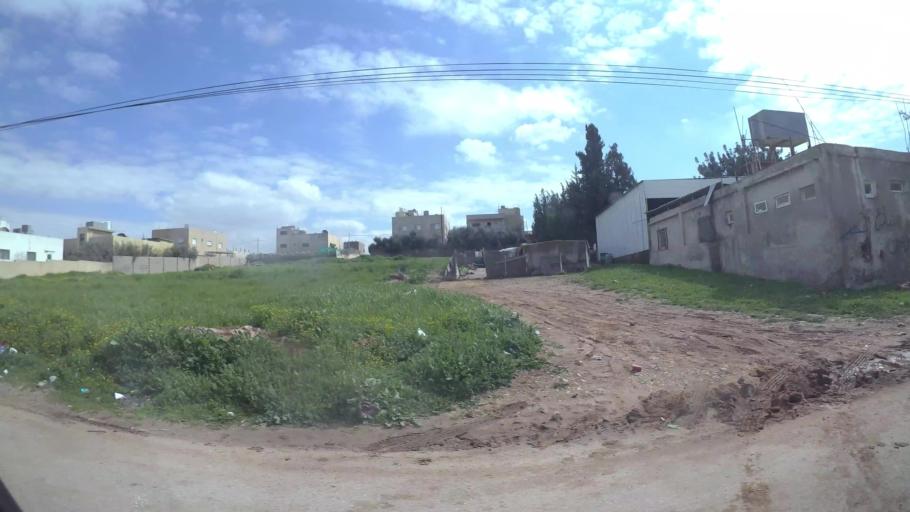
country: JO
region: Amman
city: Al Jubayhah
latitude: 32.0616
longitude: 35.8226
